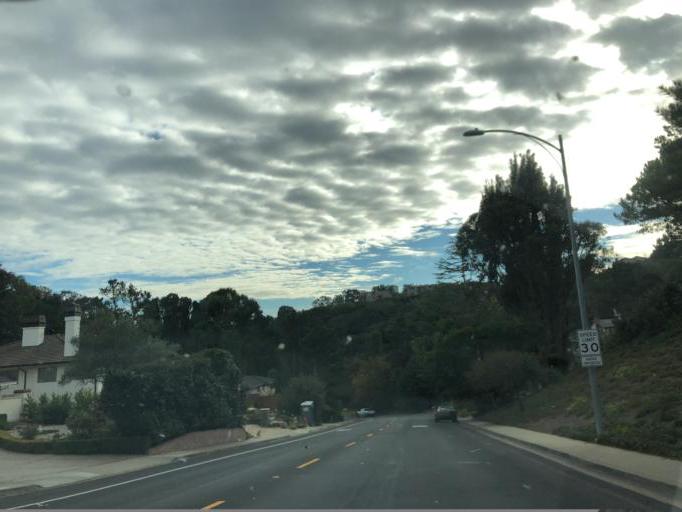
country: US
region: California
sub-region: San Mateo County
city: Highlands-Baywood Park
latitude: 37.5096
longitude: -122.3192
